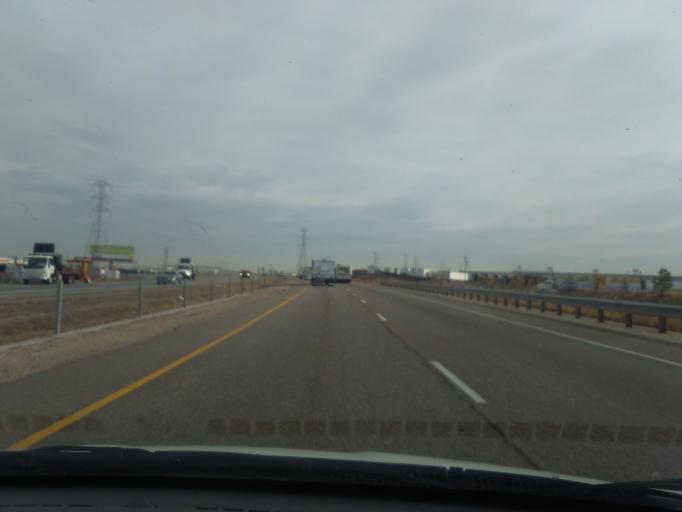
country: US
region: Colorado
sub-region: Adams County
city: Derby
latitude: 39.8813
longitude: -104.8774
